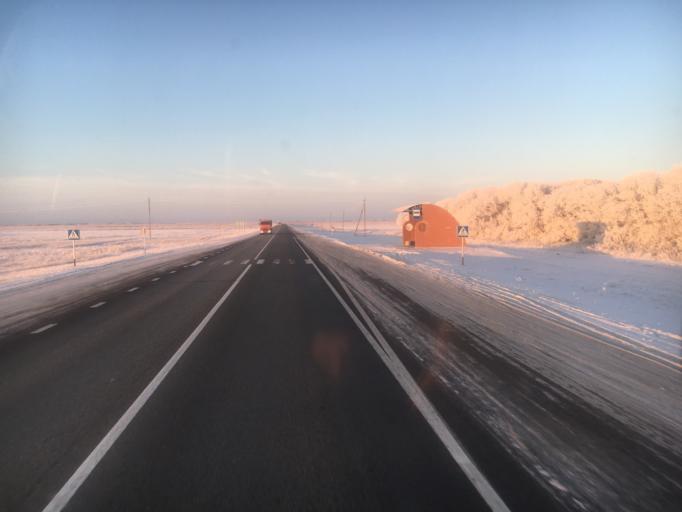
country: KZ
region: Soltustik Qazaqstan
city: Smirnovo
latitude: 54.2721
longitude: 69.1593
